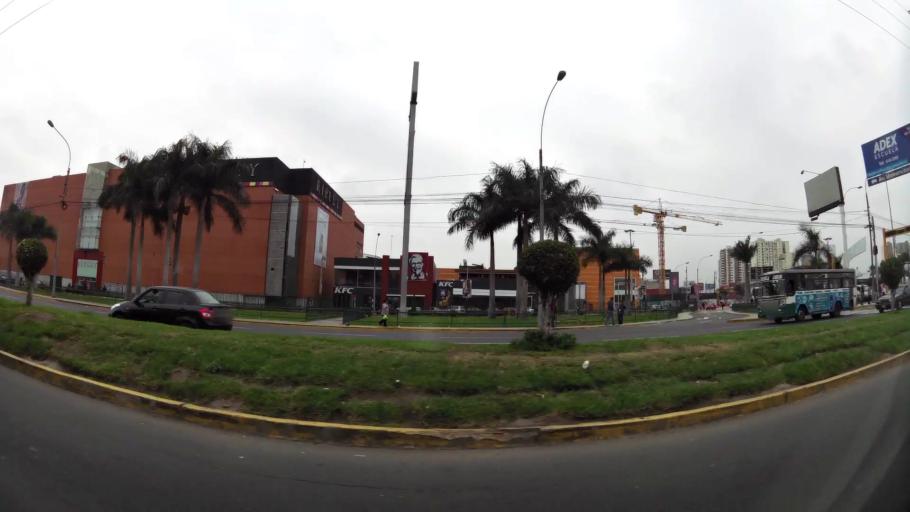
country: PE
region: Callao
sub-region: Callao
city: Callao
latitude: -12.0784
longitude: -77.0822
